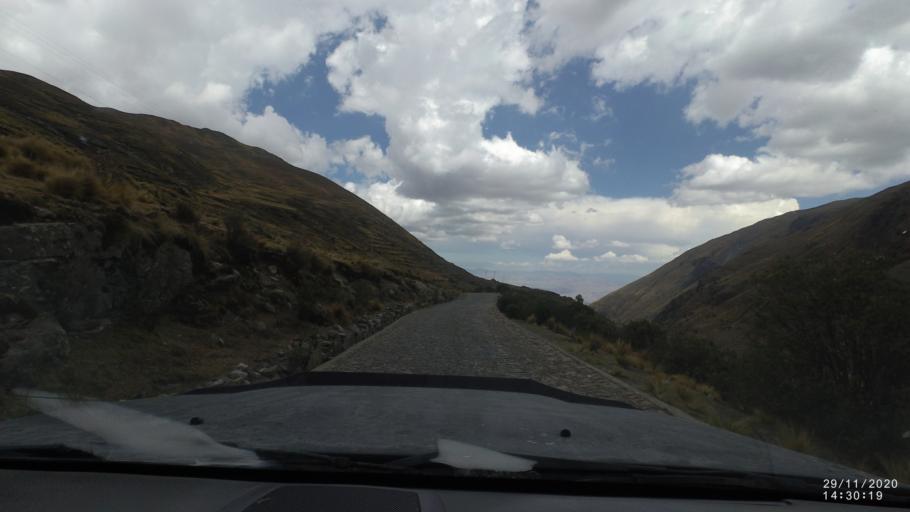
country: BO
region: Cochabamba
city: Sipe Sipe
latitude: -17.2635
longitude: -66.3497
